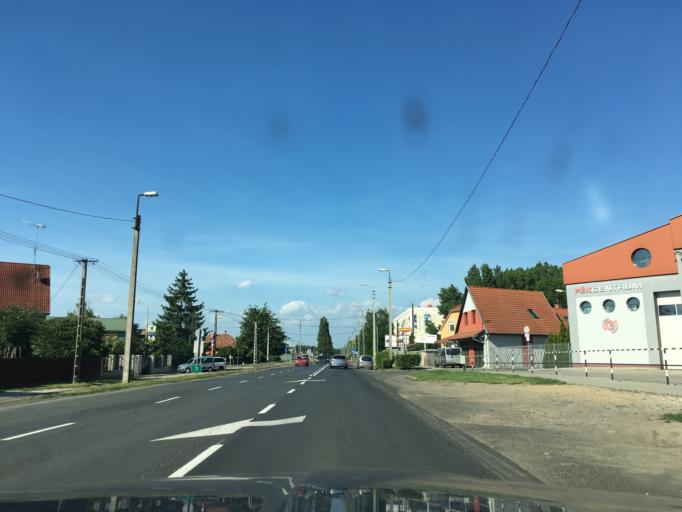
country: HU
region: Hajdu-Bihar
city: Debrecen
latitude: 47.5523
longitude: 21.6642
